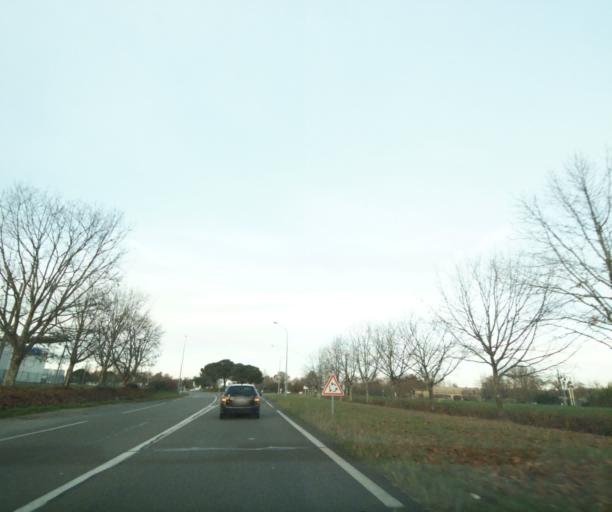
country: FR
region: Aquitaine
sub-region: Departement de la Gironde
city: Bazas
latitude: 44.4426
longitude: -0.2368
